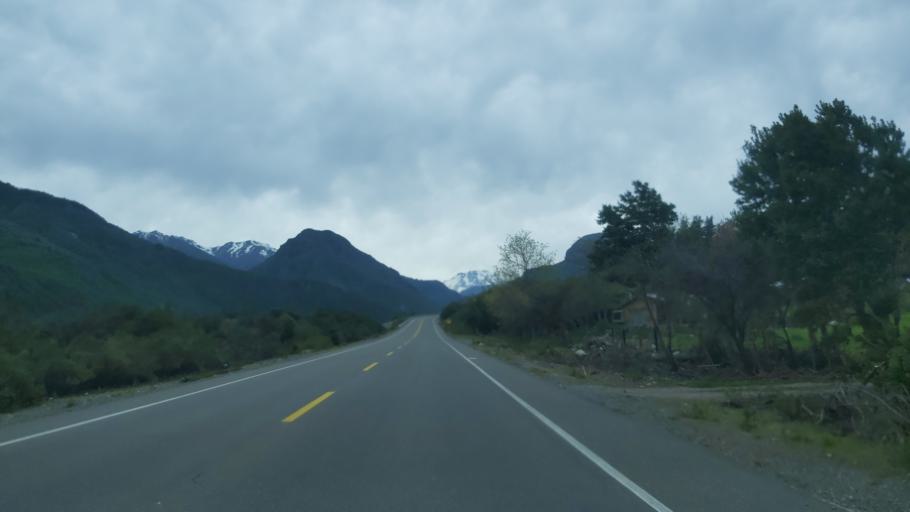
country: CL
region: Maule
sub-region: Provincia de Linares
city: Colbun
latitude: -35.7089
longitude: -71.1052
